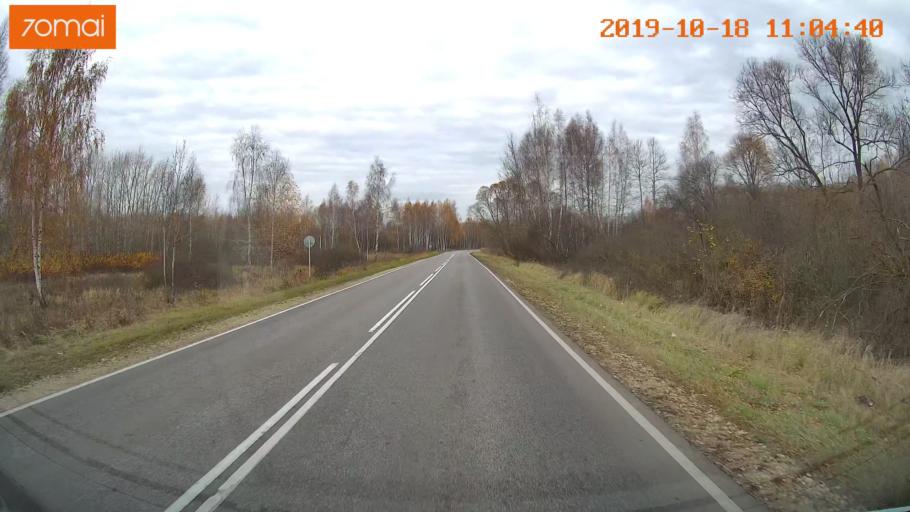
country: RU
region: Tula
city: Yepifan'
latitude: 53.8961
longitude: 38.5438
